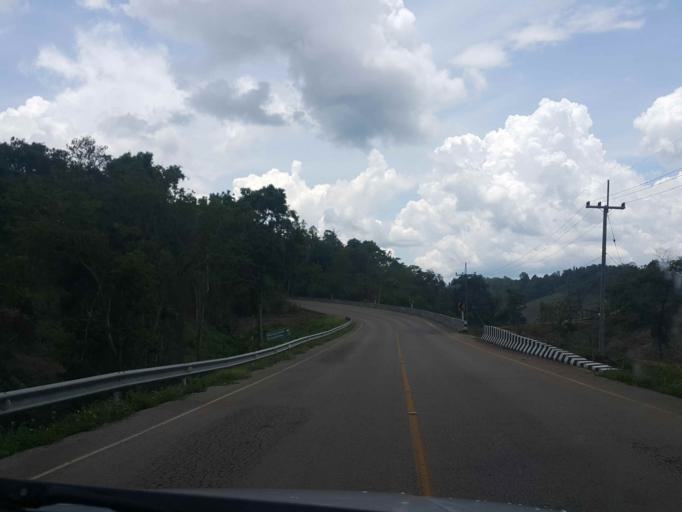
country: TH
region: Lampang
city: Ngao
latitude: 18.9309
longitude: 100.0907
